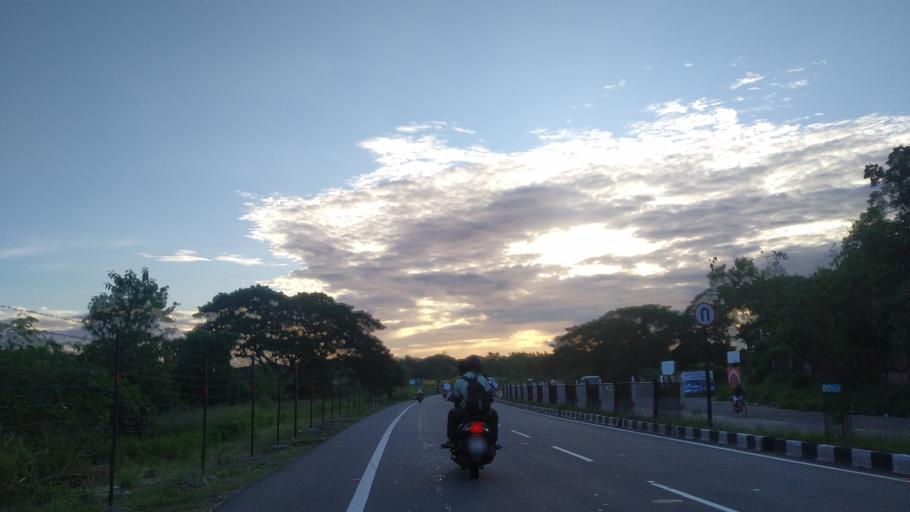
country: IN
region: Kerala
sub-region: Ernakulam
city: Elur
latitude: 10.0692
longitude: 76.3144
